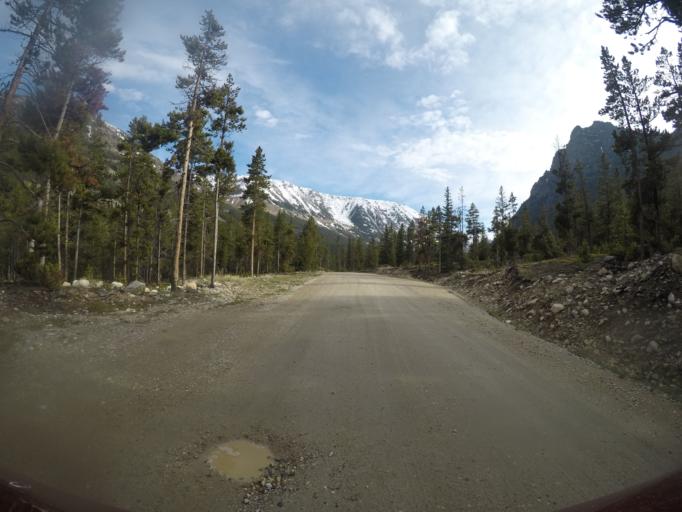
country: US
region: Montana
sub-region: Carbon County
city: Red Lodge
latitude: 45.0450
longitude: -109.4259
